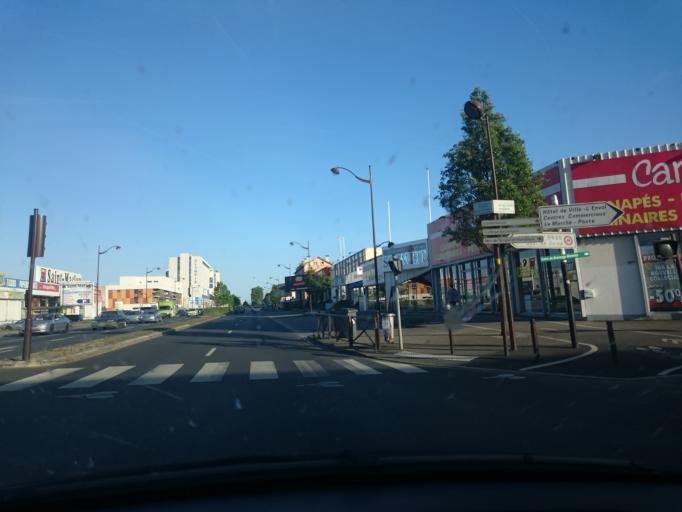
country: FR
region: Ile-de-France
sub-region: Departement de l'Essonne
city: Juvisy-sur-Orge
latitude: 48.6785
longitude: 2.3822
